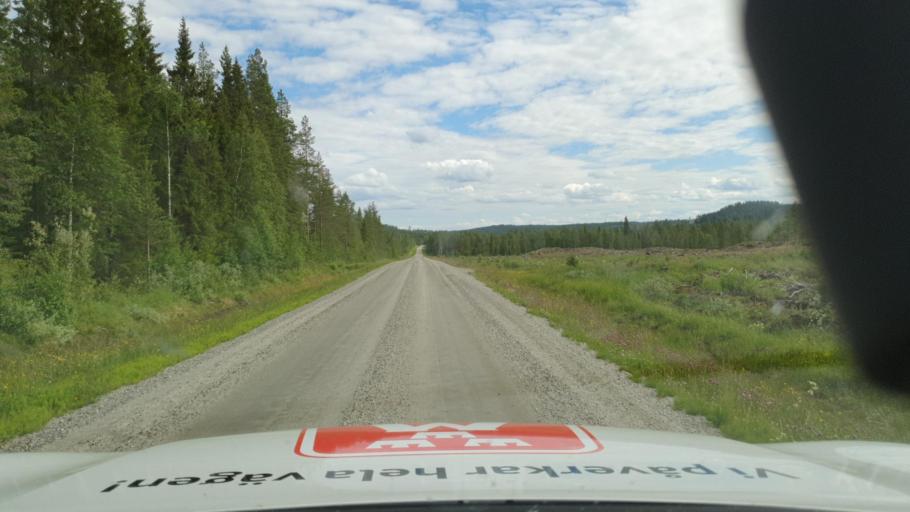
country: SE
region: Vaesterbotten
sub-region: Norsjo Kommun
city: Norsjoe
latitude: 64.8543
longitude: 19.5039
